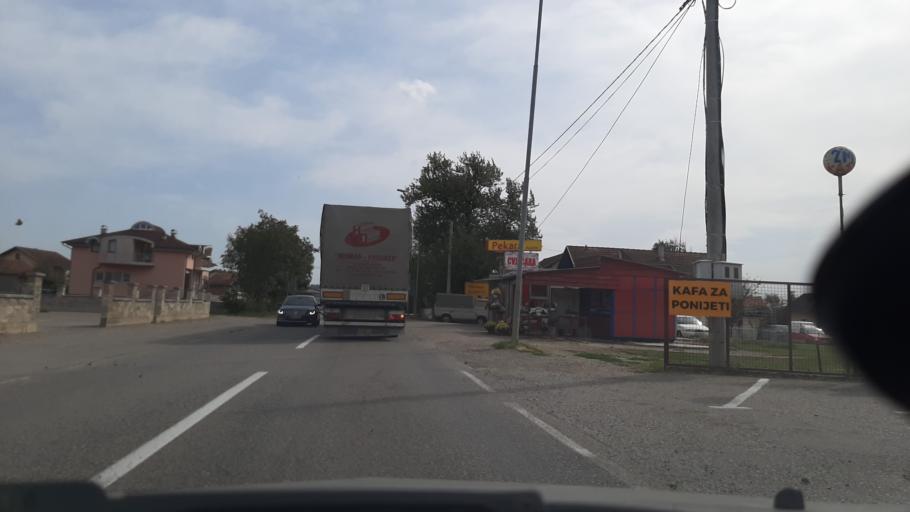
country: BA
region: Republika Srpska
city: Laktasi
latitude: 44.8787
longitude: 17.2895
